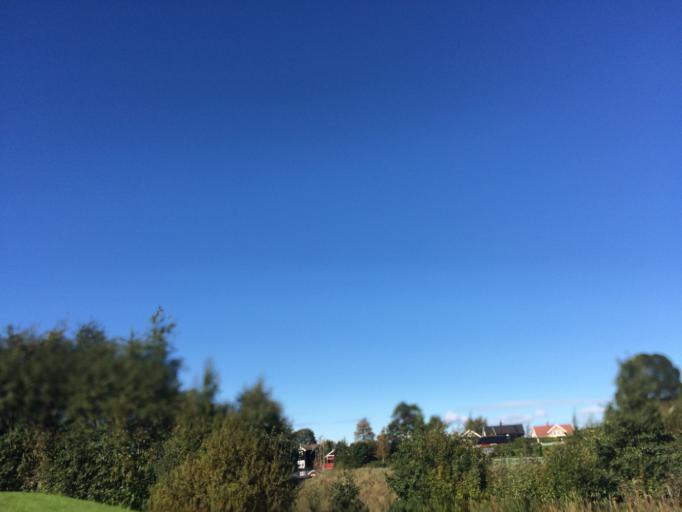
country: NO
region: Akershus
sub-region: Ski
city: Ski
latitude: 59.7230
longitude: 10.7914
